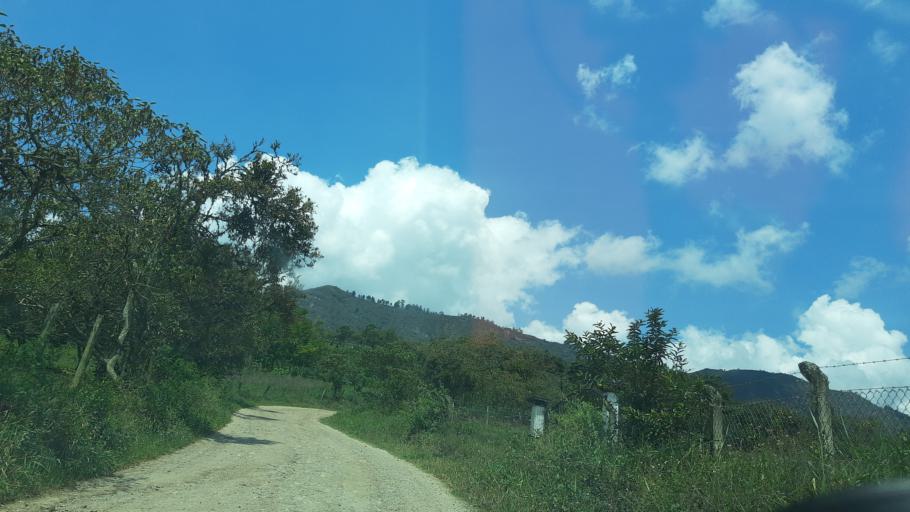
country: CO
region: Boyaca
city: Chinavita
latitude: 5.1307
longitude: -73.3693
